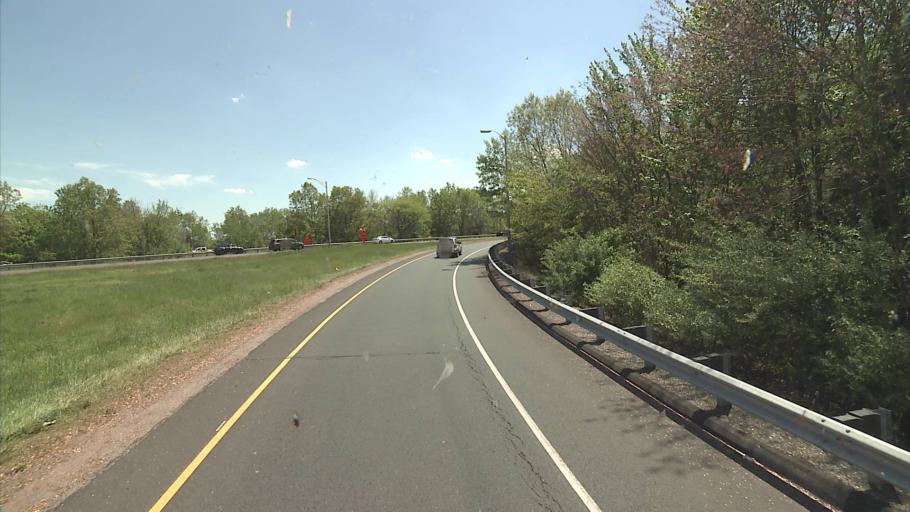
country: US
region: Connecticut
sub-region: Hartford County
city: Plainville
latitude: 41.6317
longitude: -72.8755
